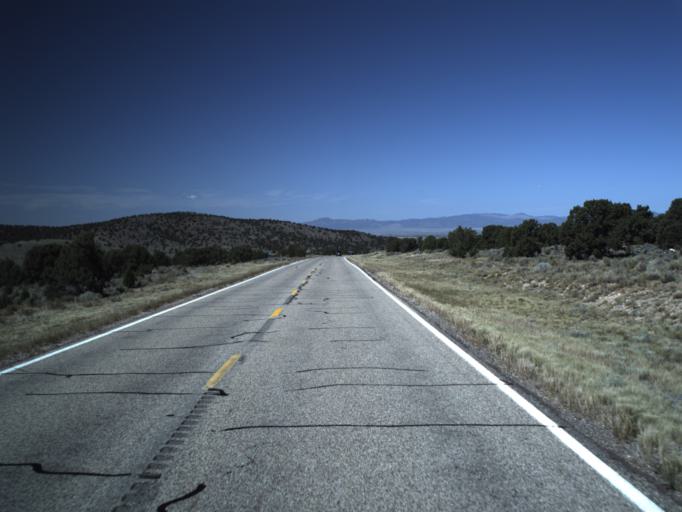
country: US
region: Utah
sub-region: Washington County
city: Enterprise
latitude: 37.6641
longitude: -113.4701
